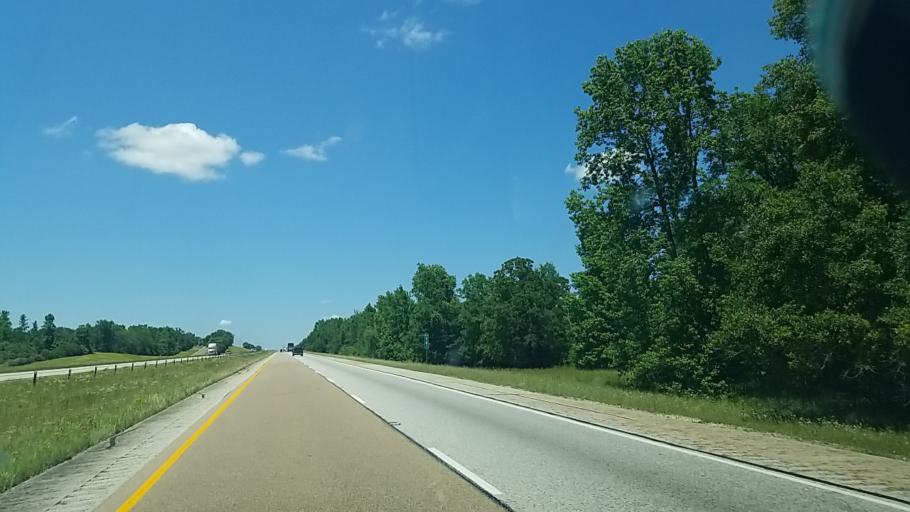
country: US
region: Texas
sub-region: Leon County
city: Centerville
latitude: 31.2138
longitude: -95.9967
